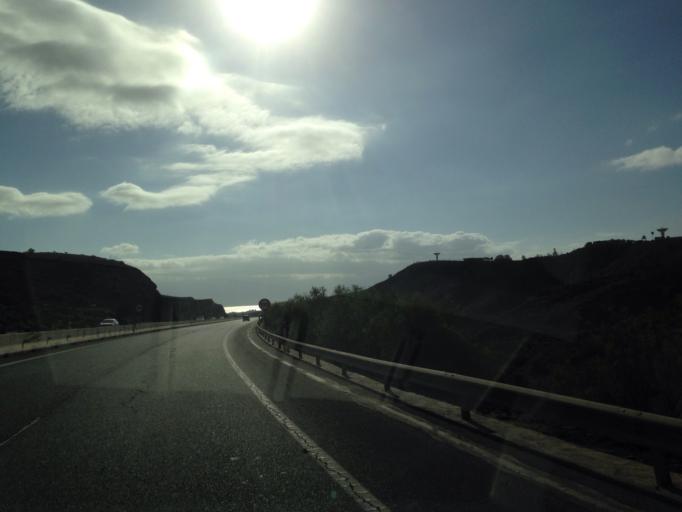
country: ES
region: Canary Islands
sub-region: Provincia de Las Palmas
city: Maspalomas
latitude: 27.7705
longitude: -15.6353
